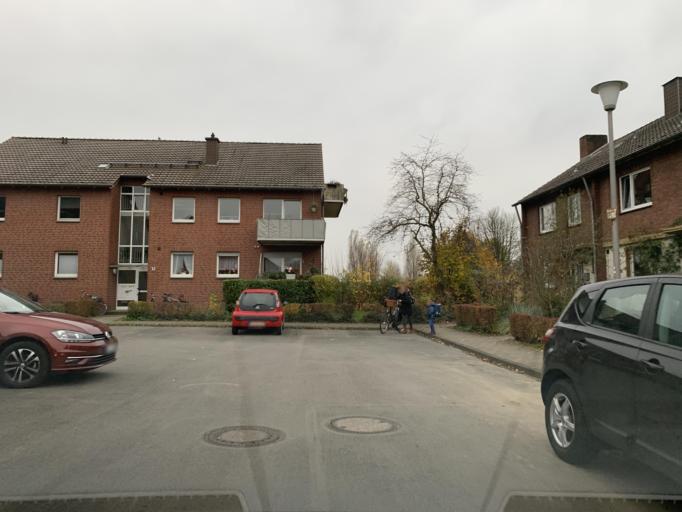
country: DE
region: North Rhine-Westphalia
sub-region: Regierungsbezirk Munster
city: Muenster
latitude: 51.9763
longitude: 7.6479
